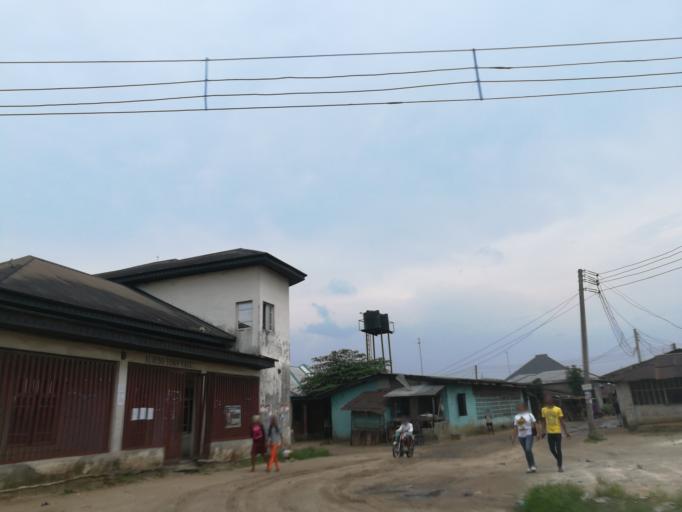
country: NG
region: Rivers
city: Okrika
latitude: 4.7870
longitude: 7.1260
